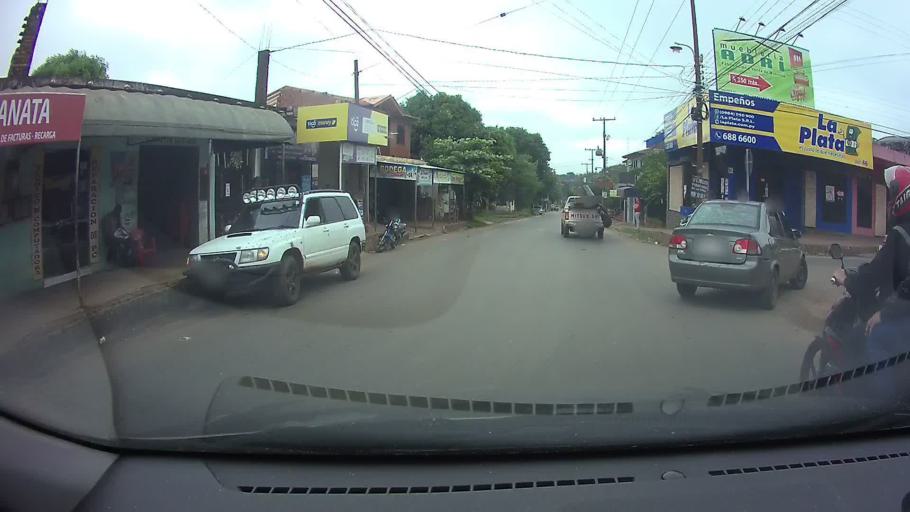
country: PY
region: Central
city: San Lorenzo
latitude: -25.3175
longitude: -57.4950
